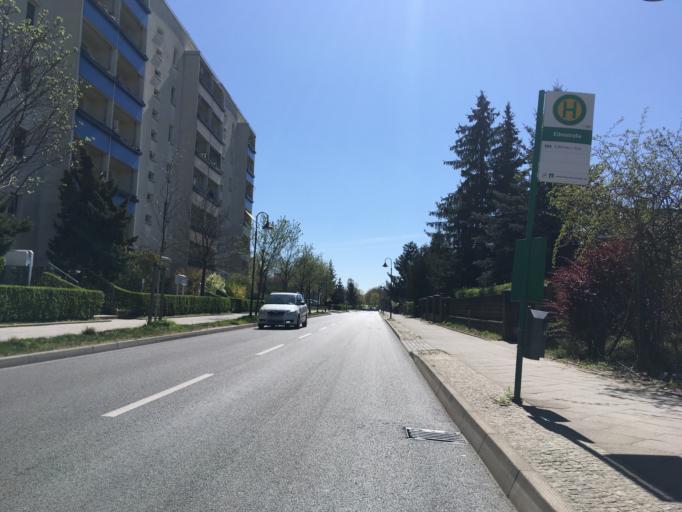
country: DE
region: Brandenburg
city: Bernau bei Berlin
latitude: 52.6708
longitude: 13.5570
